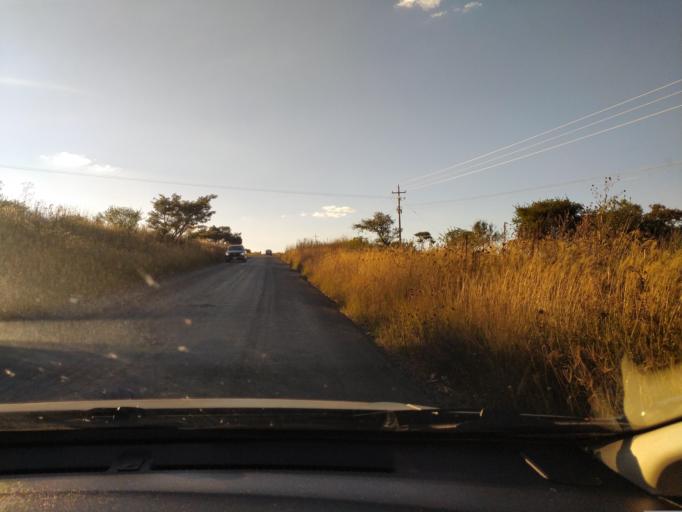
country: MX
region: Jalisco
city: San Julian
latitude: 21.0051
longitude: -102.1163
